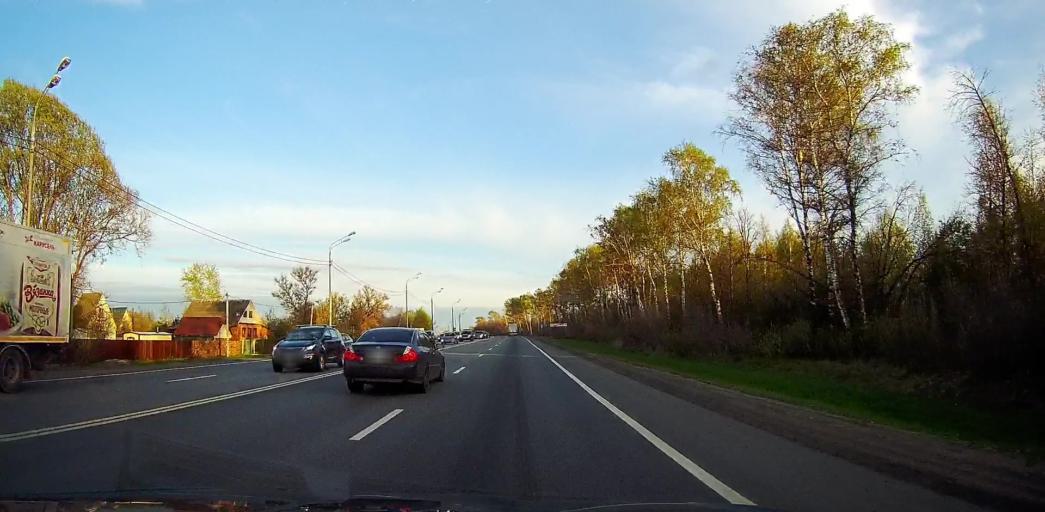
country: RU
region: Moskovskaya
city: Troitskoye
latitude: 55.2715
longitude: 38.4987
